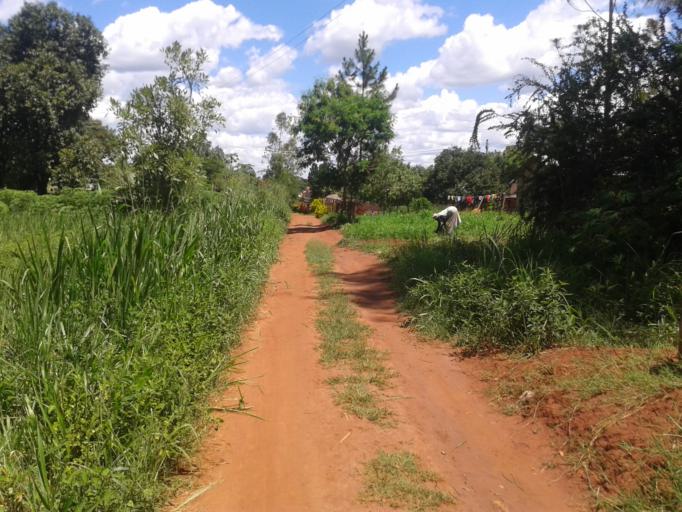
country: UG
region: Northern Region
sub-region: Gulu District
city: Gulu
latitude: 2.7707
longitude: 32.3200
